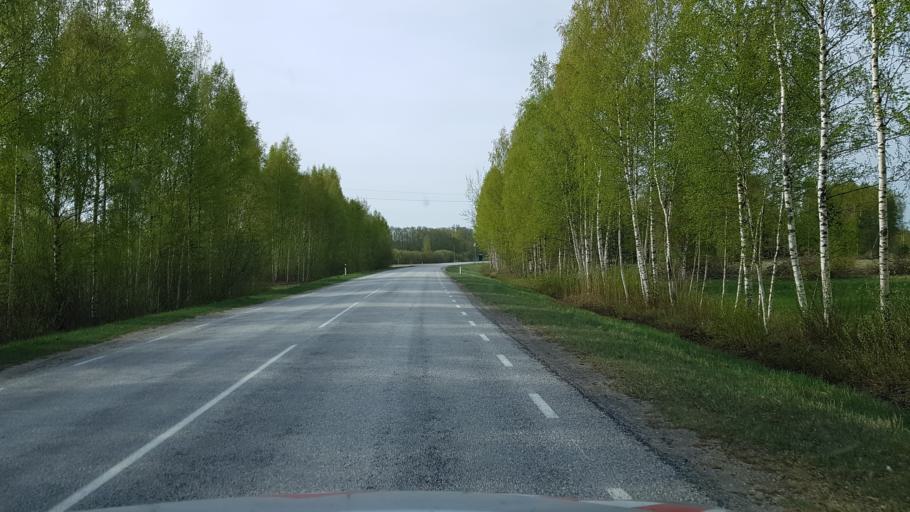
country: EE
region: Paernumaa
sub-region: Audru vald
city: Audru
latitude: 58.4079
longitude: 24.3074
